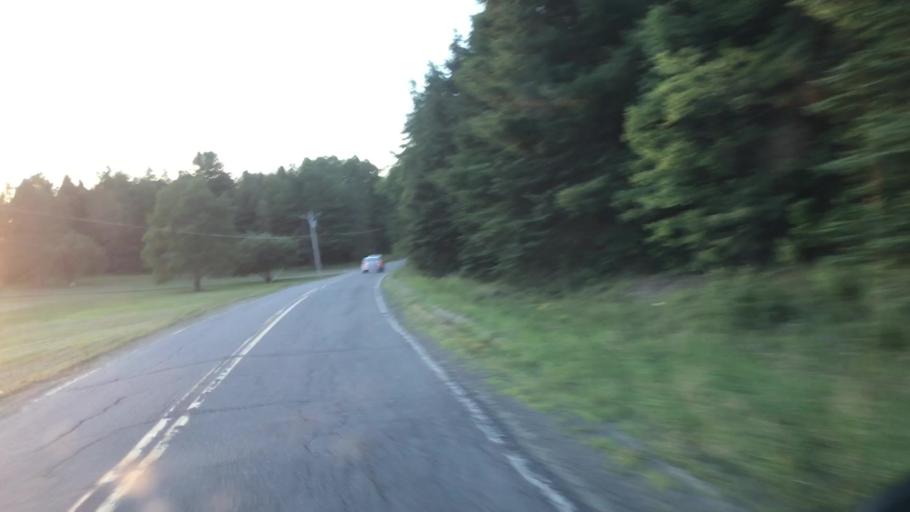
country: US
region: Maine
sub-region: Penobscot County
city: Medway
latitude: 45.6064
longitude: -68.2555
